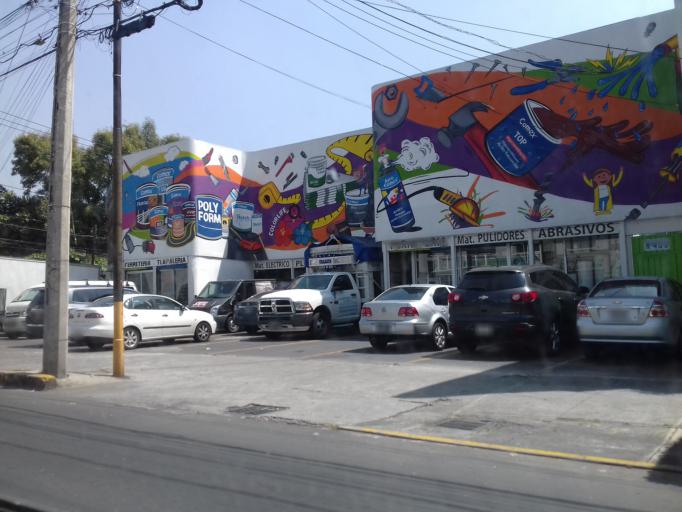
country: MX
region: Mexico City
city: Colonia del Valle
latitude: 19.3916
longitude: -99.1629
